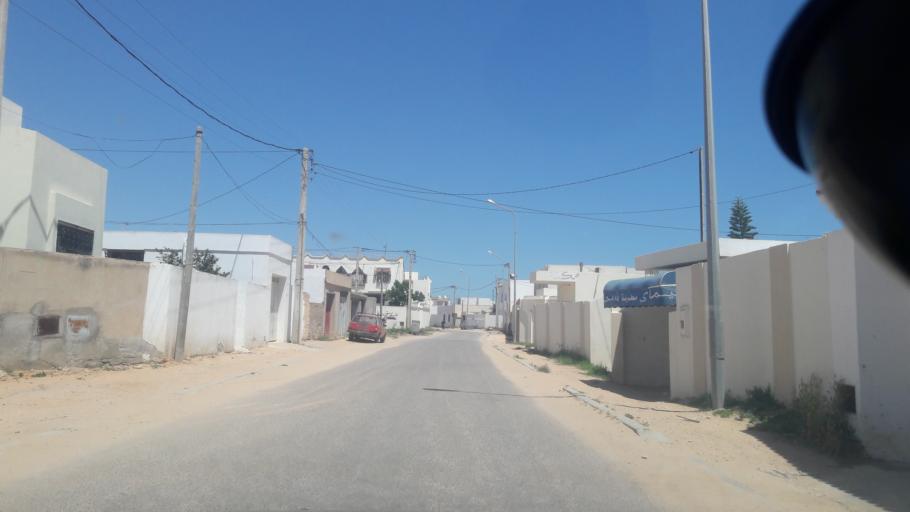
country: TN
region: Safaqis
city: Al Qarmadah
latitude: 34.8050
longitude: 10.7494
